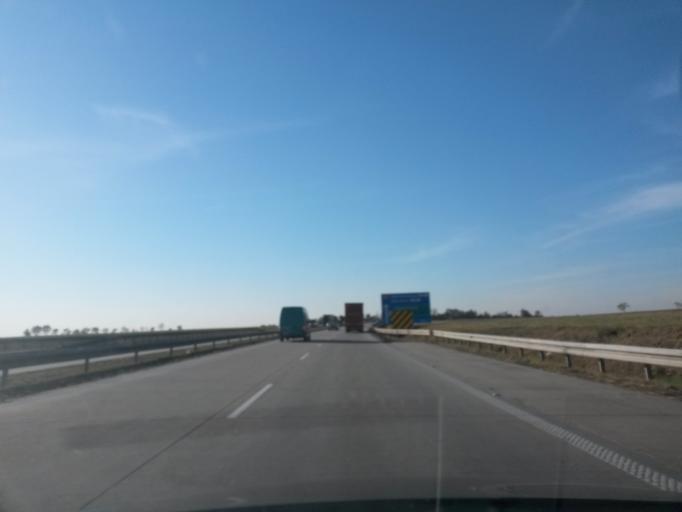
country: PL
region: Lower Silesian Voivodeship
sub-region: Powiat sredzki
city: Udanin
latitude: 51.0673
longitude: 16.4767
